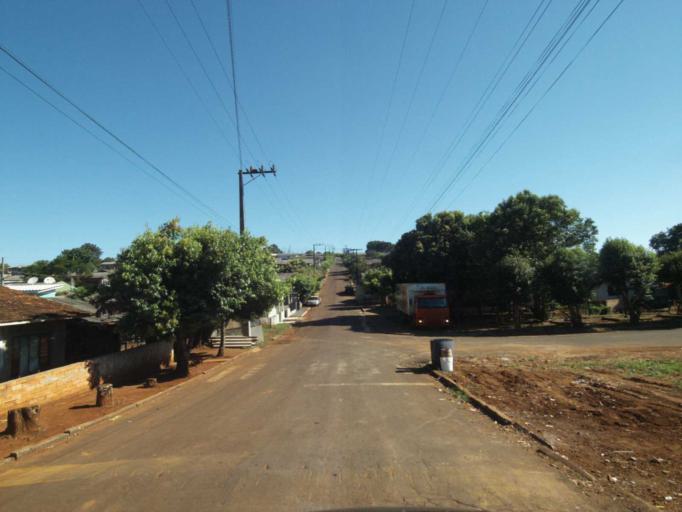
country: BR
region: Parana
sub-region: Coronel Vivida
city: Coronel Vivida
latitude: -25.9644
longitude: -52.8115
